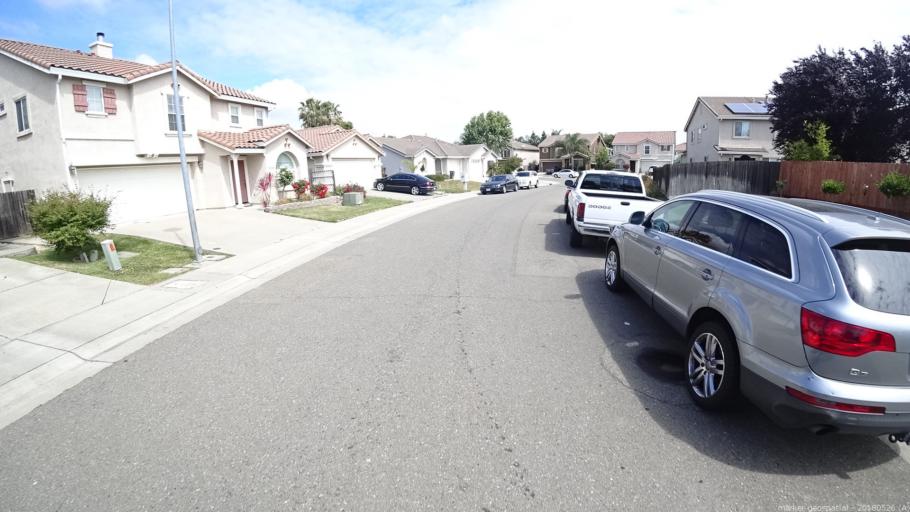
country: US
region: California
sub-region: Yolo County
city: West Sacramento
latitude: 38.6089
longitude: -121.5387
